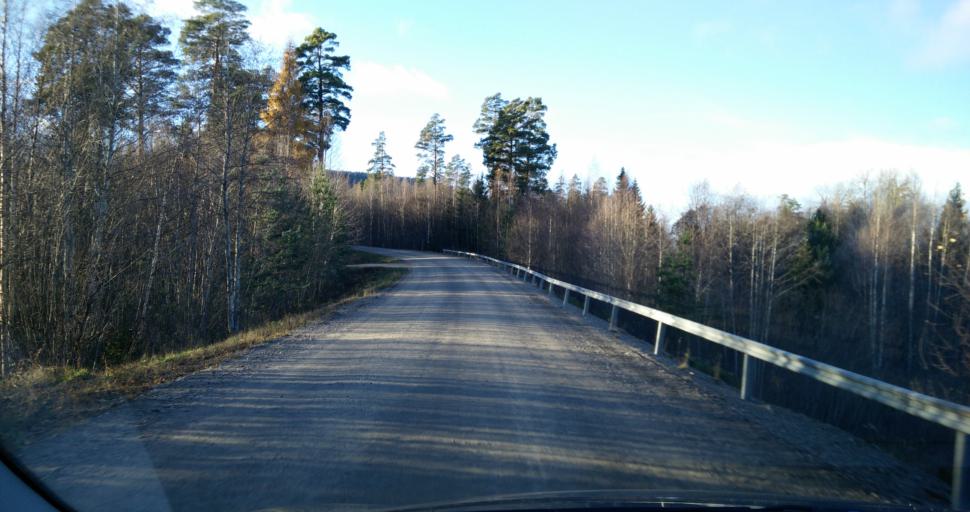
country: SE
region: Gaevleborg
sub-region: Nordanstigs Kommun
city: Bergsjoe
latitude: 62.0583
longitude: 16.7967
